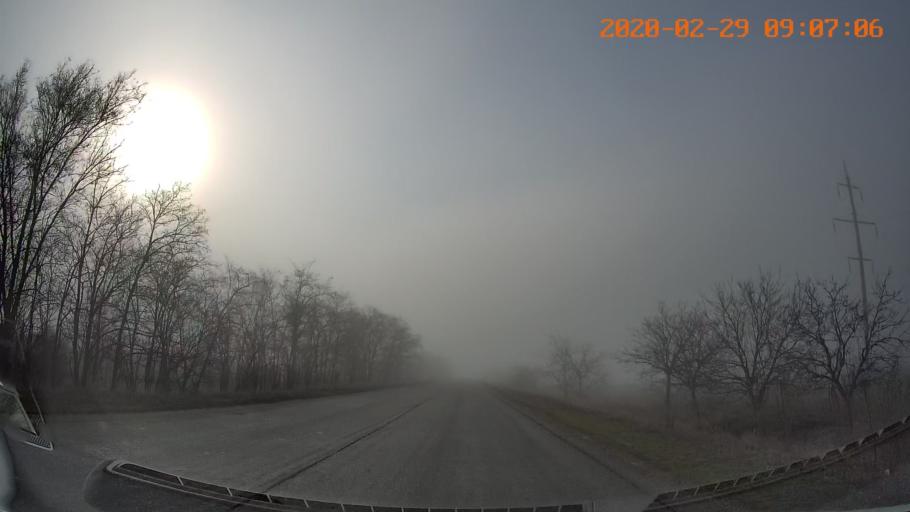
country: MD
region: Telenesti
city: Tiraspolul Nou
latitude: 46.8667
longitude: 29.7474
